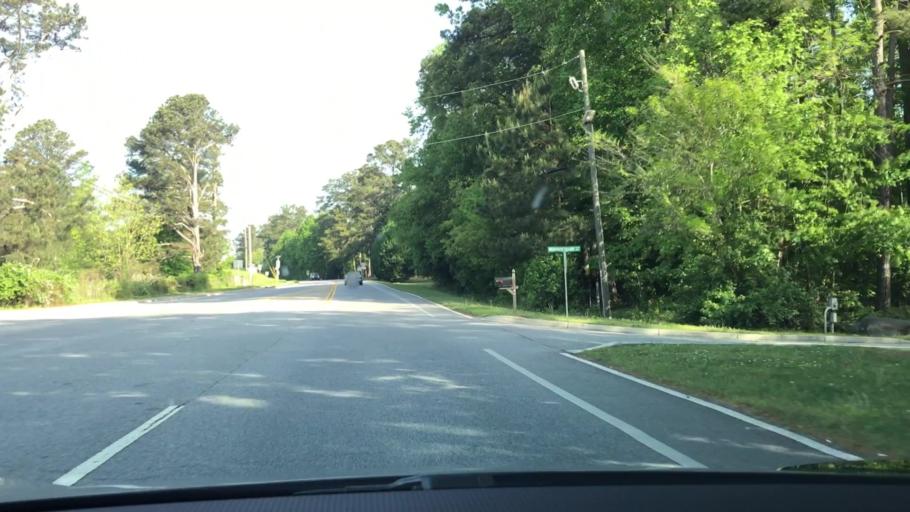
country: US
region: Georgia
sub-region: Gwinnett County
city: Sugar Hill
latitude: 34.1492
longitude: -84.0643
